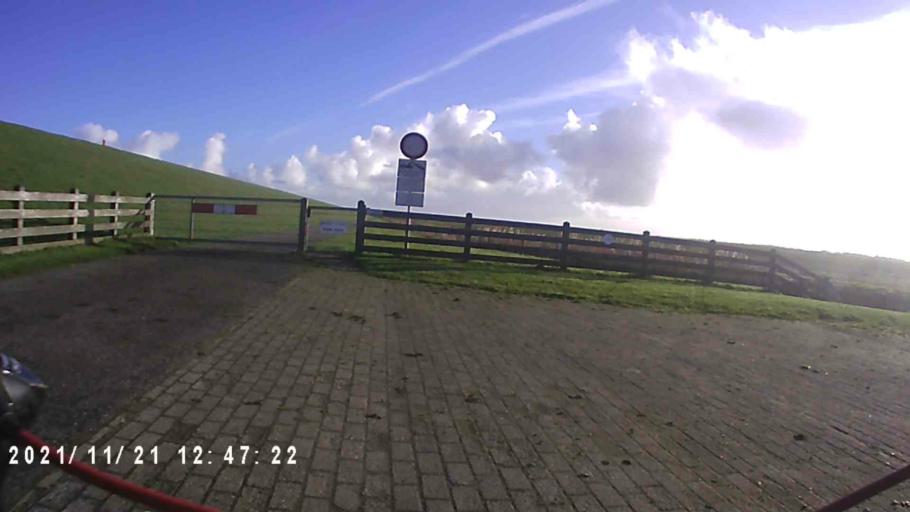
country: NL
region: Friesland
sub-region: Gemeente Dongeradeel
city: Anjum
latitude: 53.4006
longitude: 6.1098
